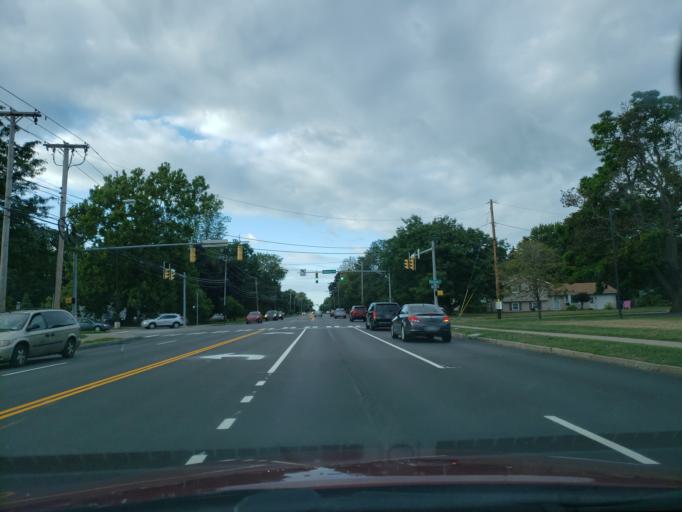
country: US
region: New York
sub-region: Monroe County
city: Greece
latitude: 43.2275
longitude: -77.6590
